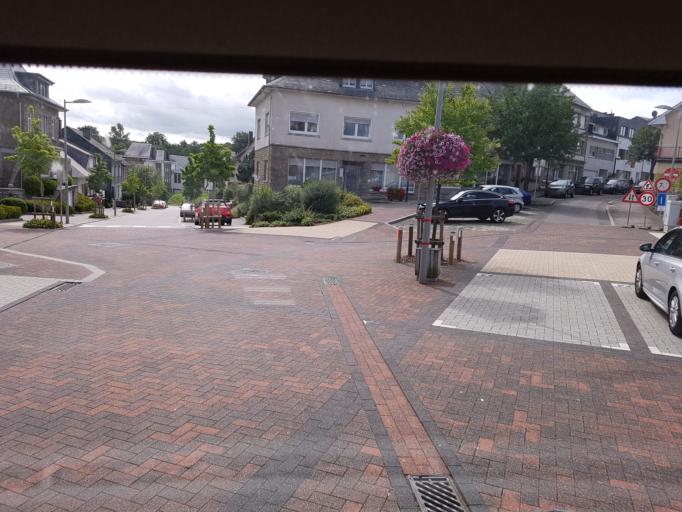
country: BE
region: Wallonia
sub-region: Province de Liege
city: Saint-Vith
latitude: 50.2813
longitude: 6.1279
